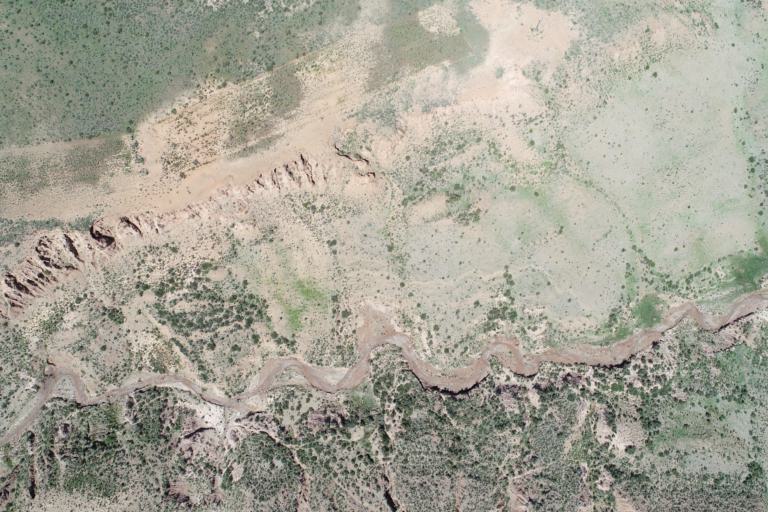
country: BO
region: La Paz
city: Curahuara de Carangas
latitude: -17.3234
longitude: -68.5067
